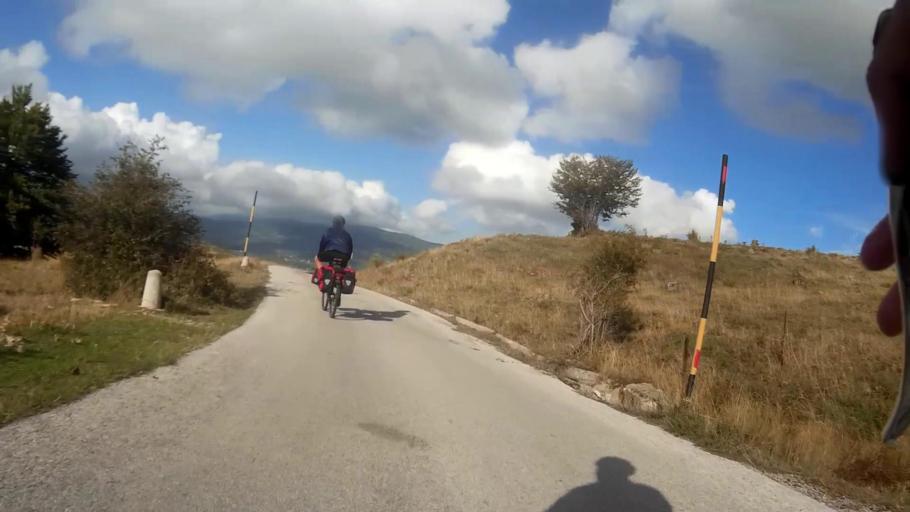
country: IT
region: Basilicate
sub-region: Provincia di Potenza
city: Viggianello
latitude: 39.9577
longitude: 16.1415
